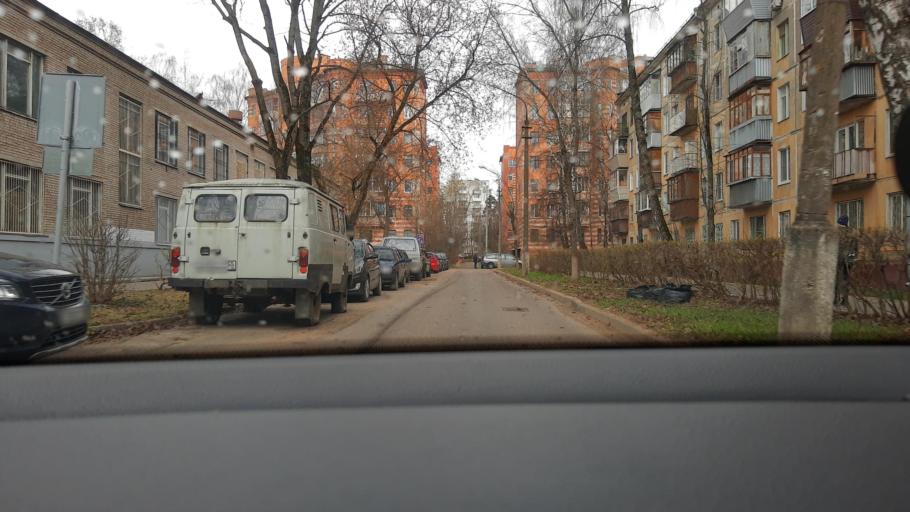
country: RU
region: Moskovskaya
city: Bolshevo
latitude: 55.9291
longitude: 37.8202
